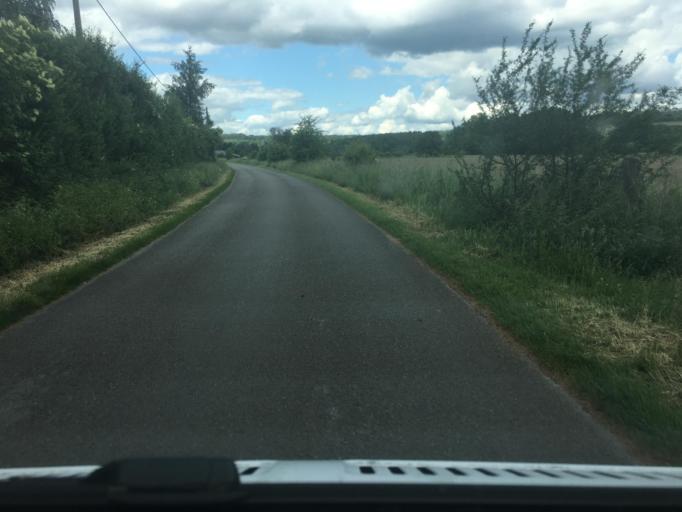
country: BE
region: Wallonia
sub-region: Province du Luxembourg
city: Florenville
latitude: 49.7151
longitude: 5.2599
